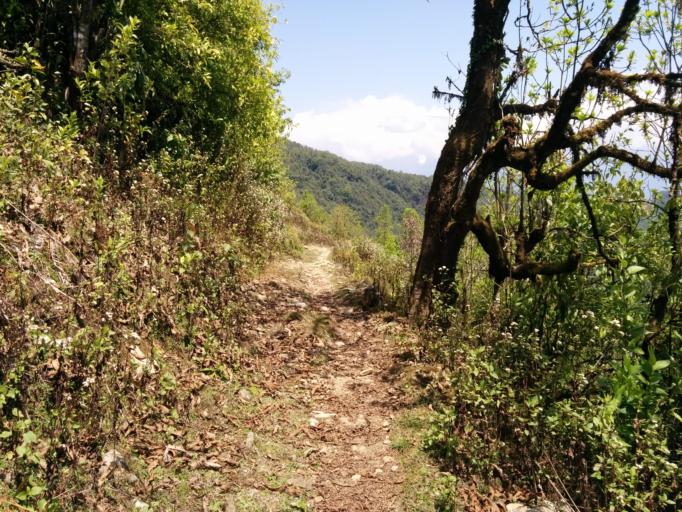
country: NP
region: Western Region
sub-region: Gandaki Zone
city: Pokhara
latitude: 28.2227
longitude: 83.8094
